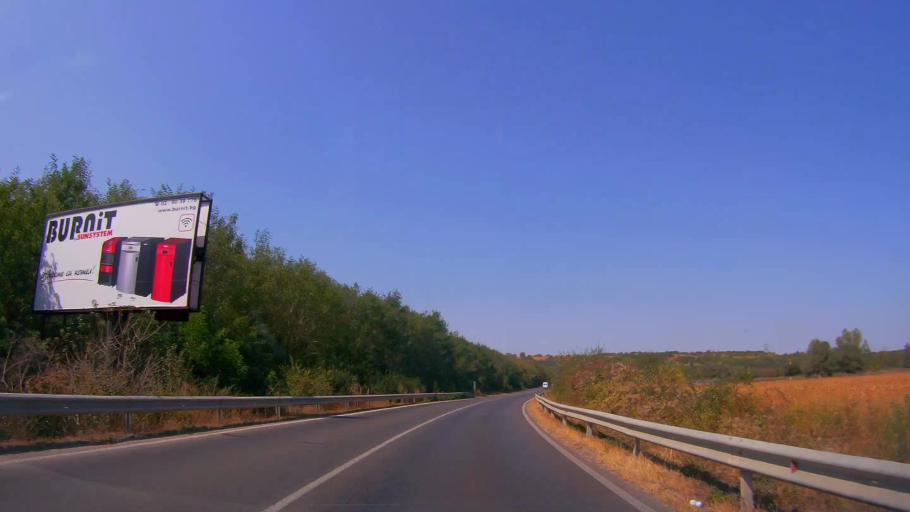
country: BG
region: Razgrad
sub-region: Obshtina Tsar Kaloyan
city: Tsar Kaloyan
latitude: 43.6156
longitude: 26.2149
